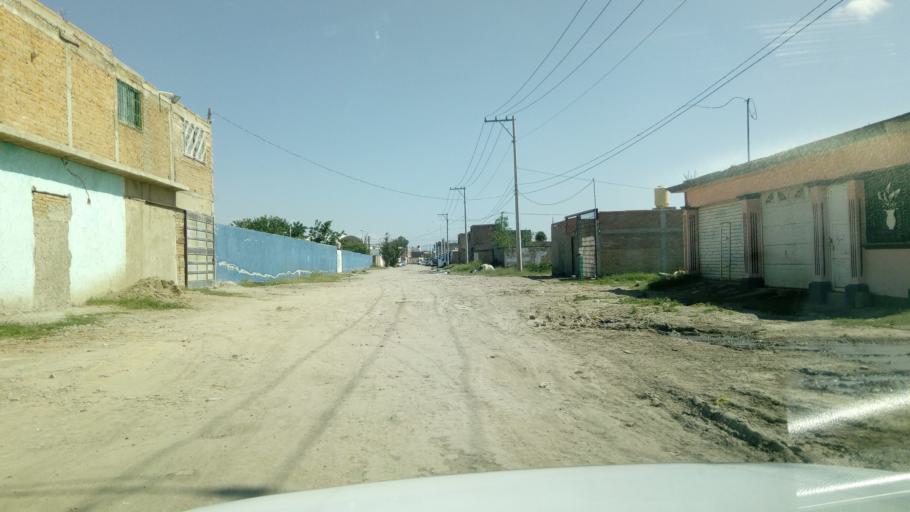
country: MX
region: Durango
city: Victoria de Durango
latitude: 23.9889
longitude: -104.6814
